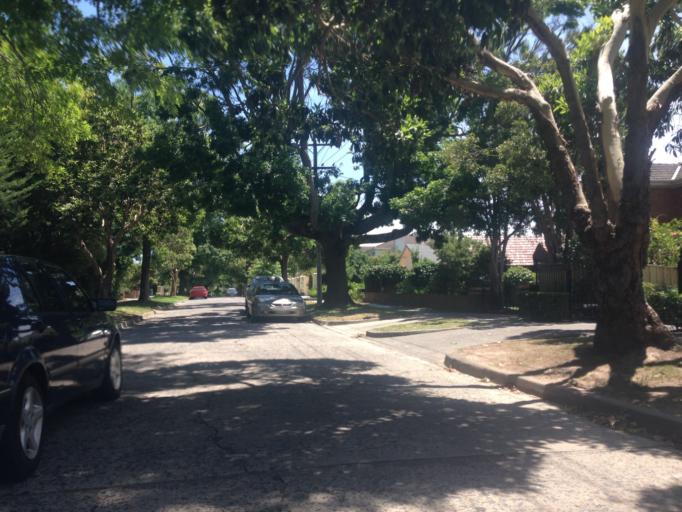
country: AU
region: Victoria
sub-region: Boroondara
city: Kew East
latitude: -37.7916
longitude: 145.0698
